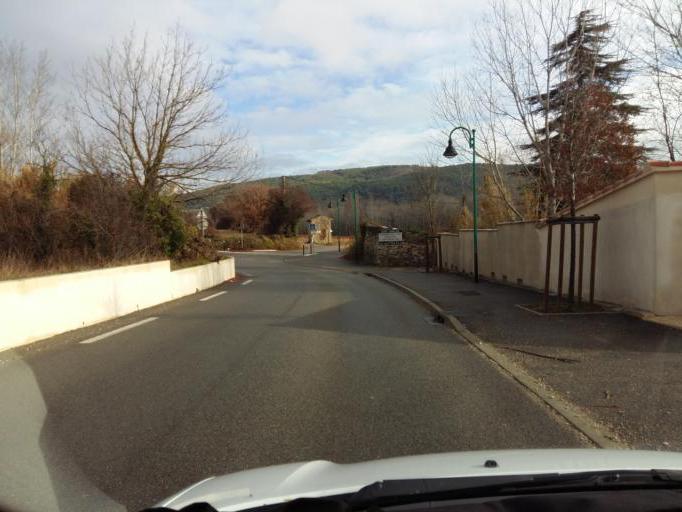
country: FR
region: Provence-Alpes-Cote d'Azur
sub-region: Departement du Vaucluse
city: Vaison-la-Romaine
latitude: 44.2398
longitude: 5.0885
